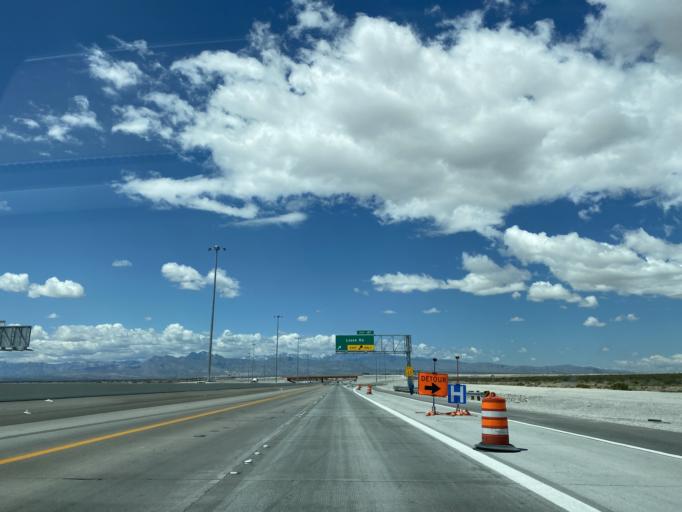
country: US
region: Nevada
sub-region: Clark County
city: Nellis Air Force Base
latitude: 36.2898
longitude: -115.1092
